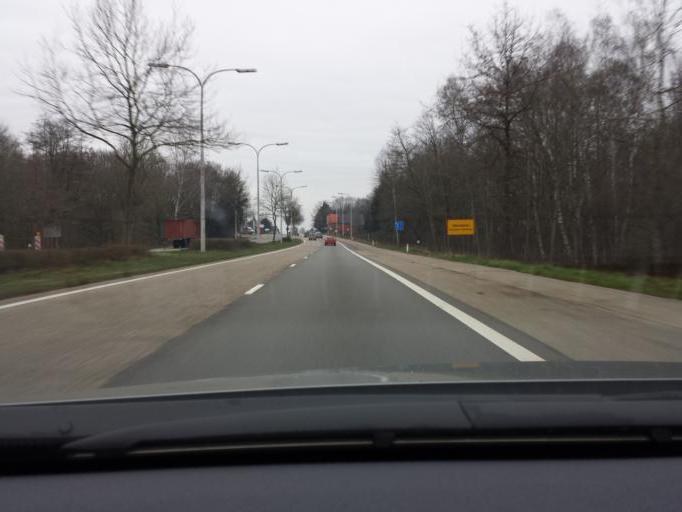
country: BE
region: Flanders
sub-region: Provincie Limburg
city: Helchteren
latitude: 51.0472
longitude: 5.3809
